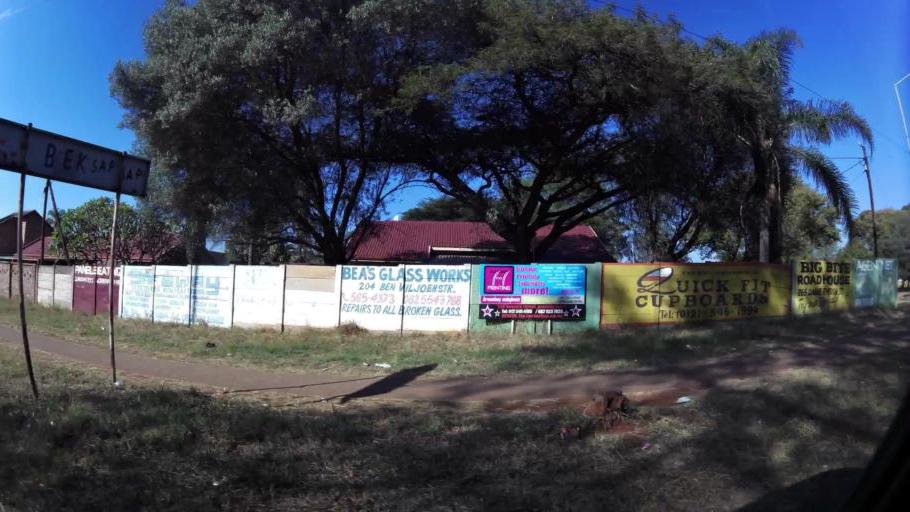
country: ZA
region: Gauteng
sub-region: City of Tshwane Metropolitan Municipality
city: Pretoria
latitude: -25.6649
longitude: 28.1554
